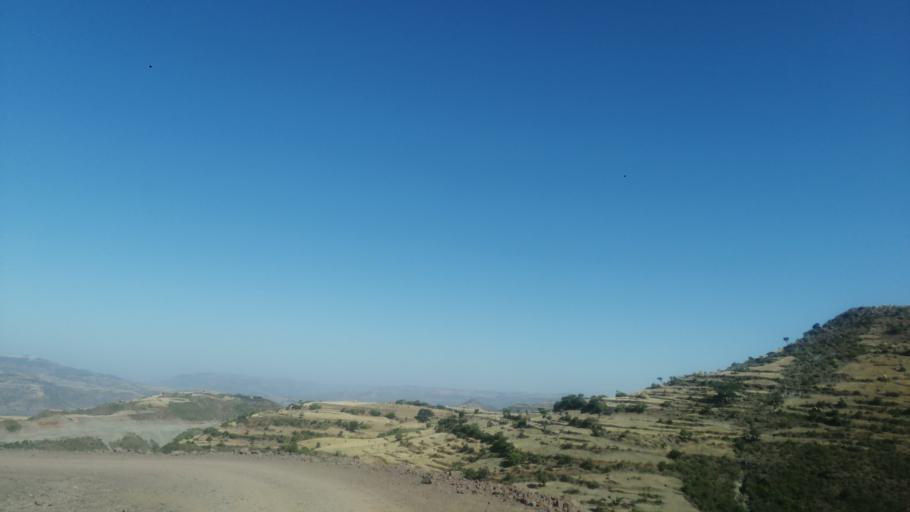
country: ET
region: Amhara
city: Addiet Canna
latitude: 11.1544
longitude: 37.8510
